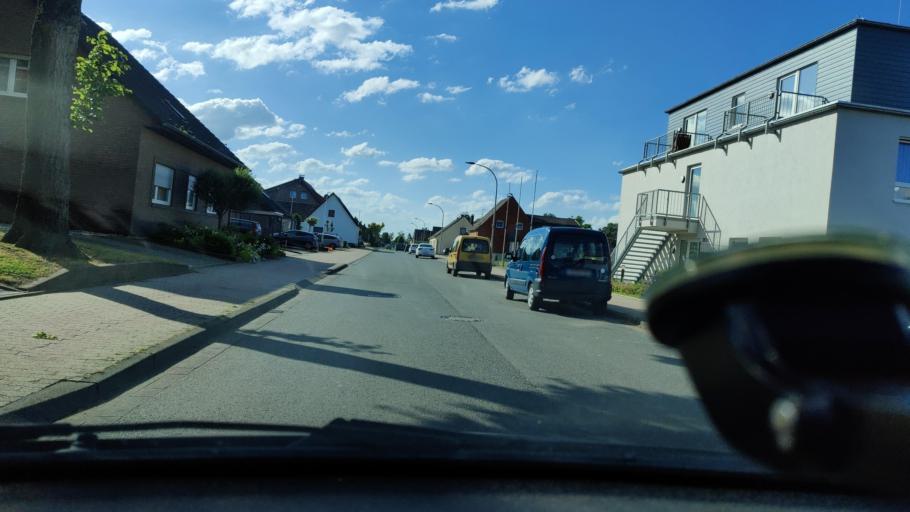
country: DE
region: North Rhine-Westphalia
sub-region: Regierungsbezirk Dusseldorf
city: Alpen
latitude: 51.5602
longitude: 6.5445
